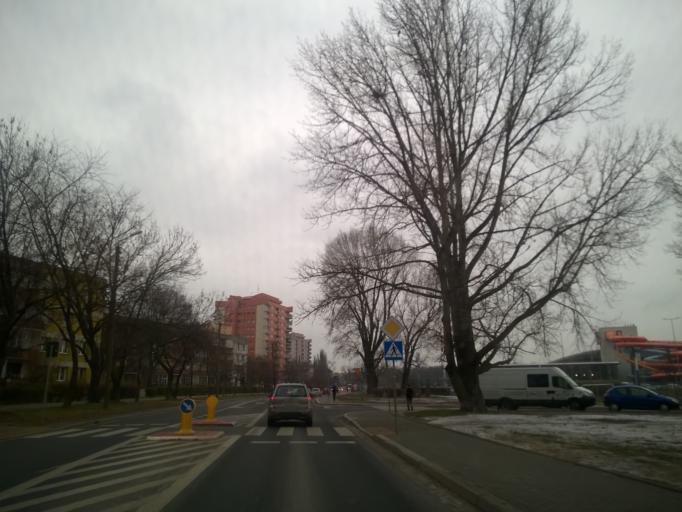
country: PL
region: Lower Silesian Voivodeship
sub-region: Powiat wroclawski
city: Wroclaw
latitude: 51.0931
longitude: 17.0335
